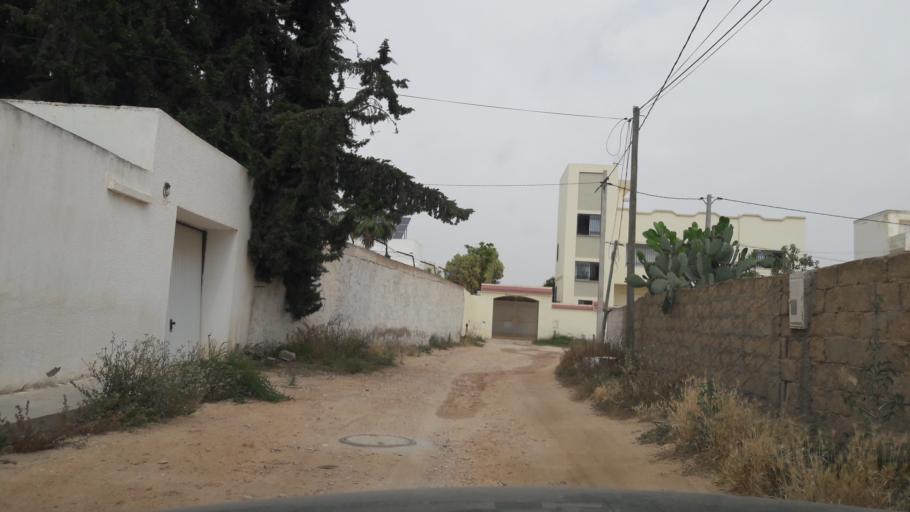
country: TN
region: Safaqis
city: Sfax
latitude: 34.7732
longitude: 10.7585
